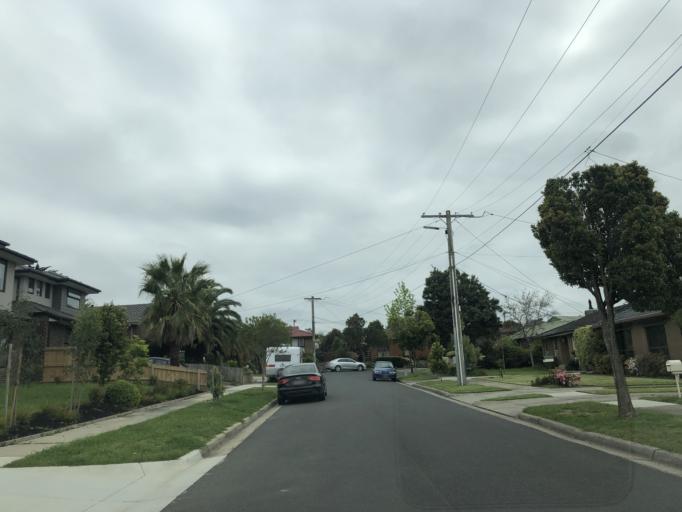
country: AU
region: Victoria
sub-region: Monash
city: Notting Hill
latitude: -37.9135
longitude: 145.1683
